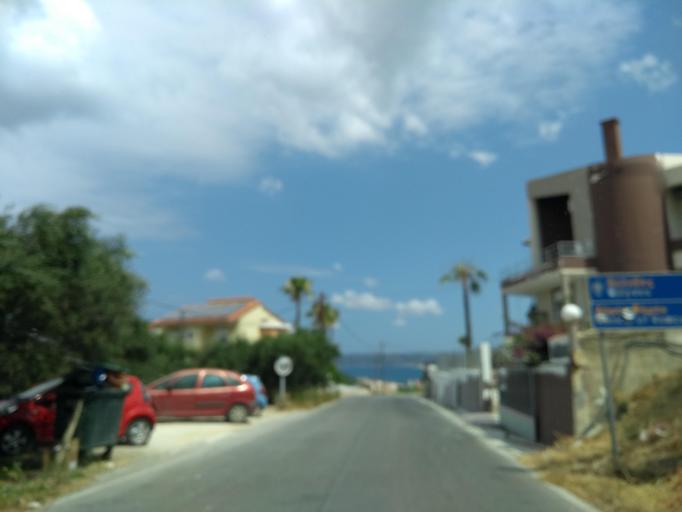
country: GR
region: Crete
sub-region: Nomos Chanias
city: Kalivai
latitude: 35.4476
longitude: 24.1756
